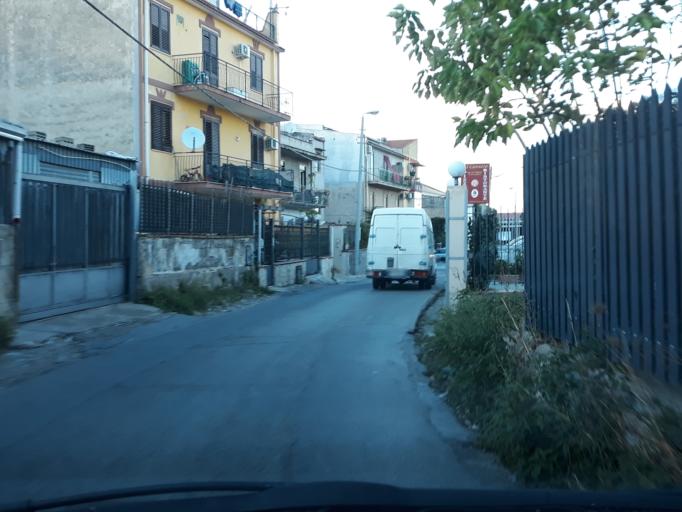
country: IT
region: Sicily
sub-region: Palermo
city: Villa Ciambra
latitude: 38.0774
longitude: 13.3122
